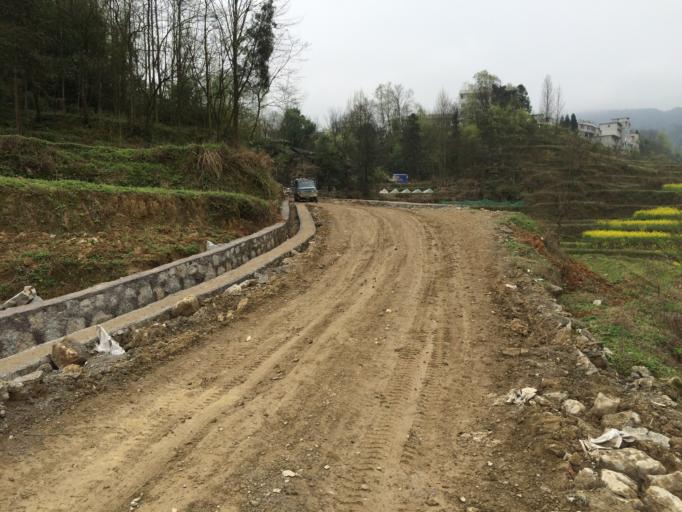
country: CN
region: Guizhou Sheng
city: Changfeng
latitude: 28.4899
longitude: 108.0616
